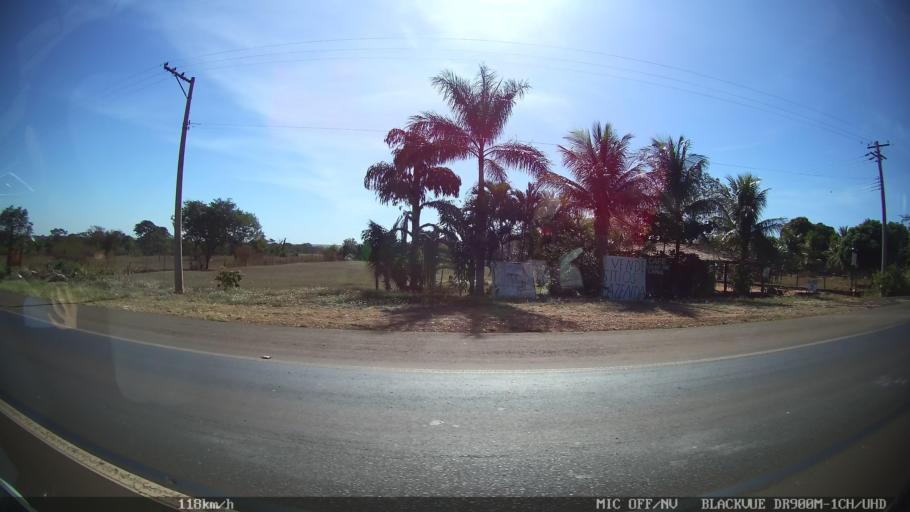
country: BR
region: Sao Paulo
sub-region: Barretos
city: Barretos
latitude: -20.5446
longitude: -48.6226
